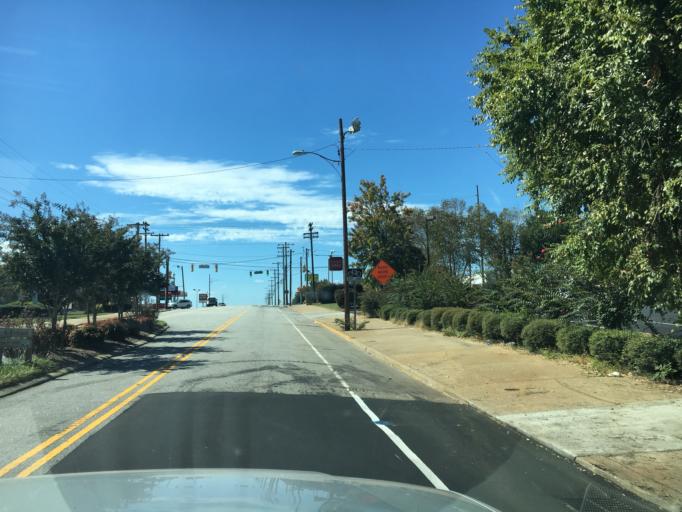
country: US
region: South Carolina
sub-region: Spartanburg County
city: Spartanburg
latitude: 34.9471
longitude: -81.9391
